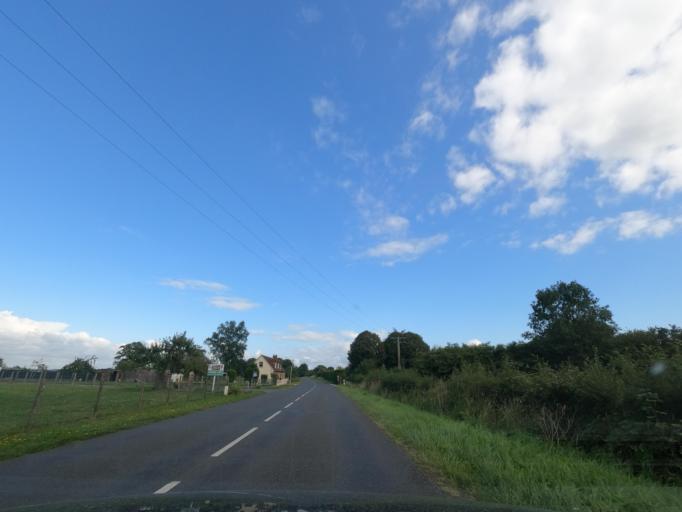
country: FR
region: Lower Normandy
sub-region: Departement de l'Orne
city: Gace
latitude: 48.7564
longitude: 0.2048
